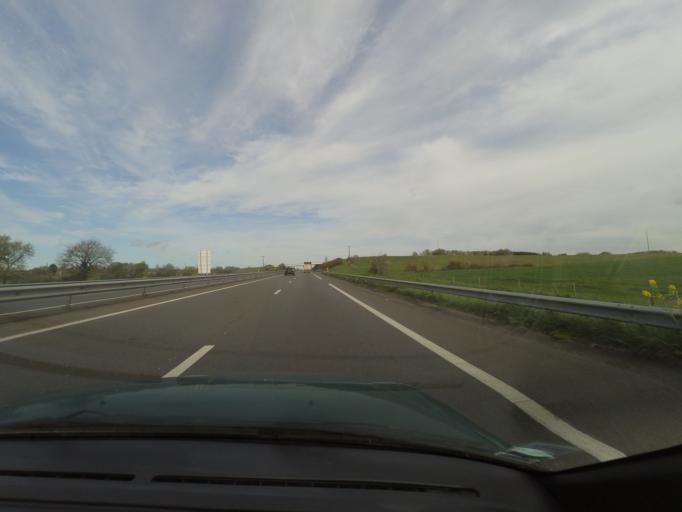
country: FR
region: Pays de la Loire
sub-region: Departement de la Loire-Atlantique
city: Le Bignon
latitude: 47.0862
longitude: -1.4534
